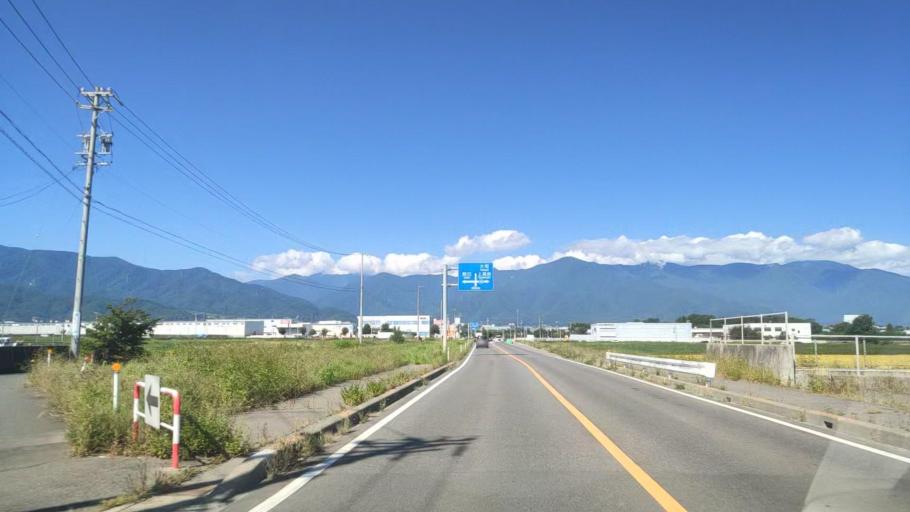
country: JP
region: Nagano
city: Matsumoto
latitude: 36.1813
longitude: 137.9080
